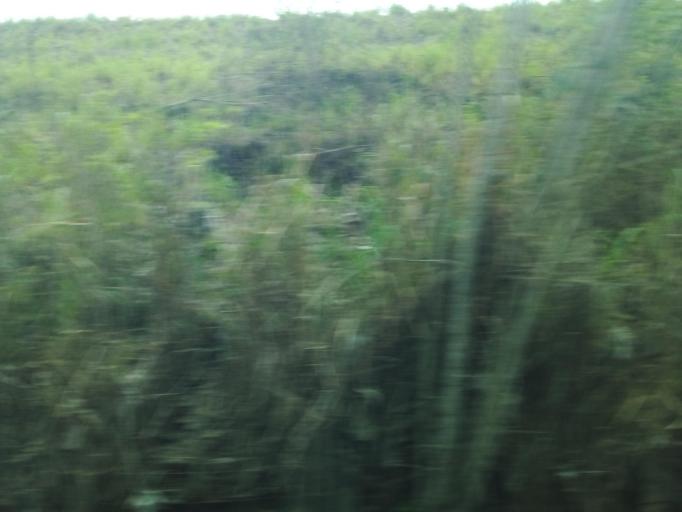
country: BR
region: Minas Gerais
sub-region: Ipatinga
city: Ipatinga
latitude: -19.4634
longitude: -42.4713
